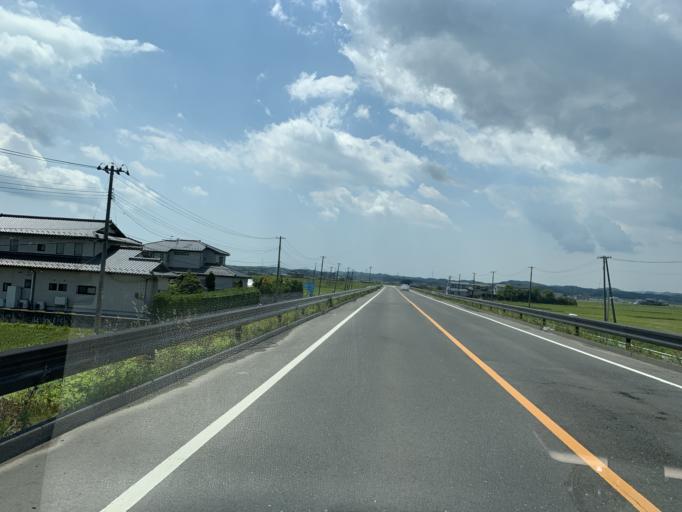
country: JP
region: Miyagi
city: Matsushima
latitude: 38.4580
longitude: 141.0866
